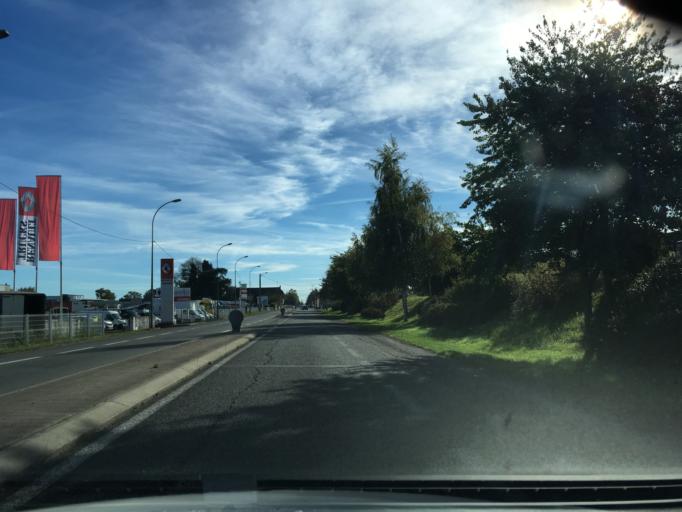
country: FR
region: Aquitaine
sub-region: Departement des Pyrenees-Atlantiques
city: Idron
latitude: 43.3044
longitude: -0.3259
